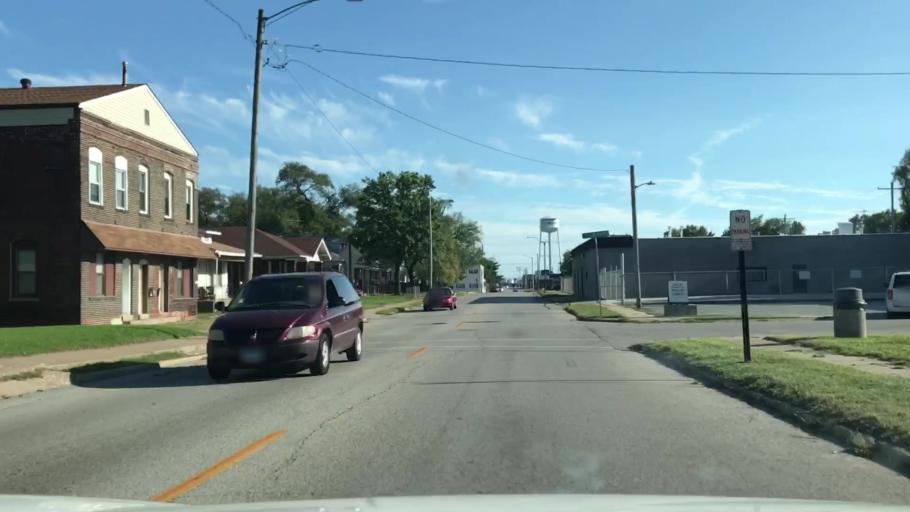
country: US
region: Illinois
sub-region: Madison County
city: Wood River
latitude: 38.8655
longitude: -90.0985
